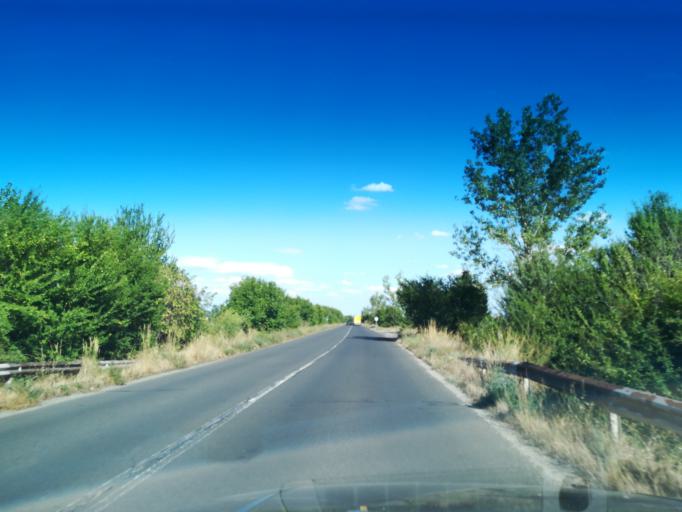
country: BG
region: Stara Zagora
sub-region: Obshtina Chirpan
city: Chirpan
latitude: 42.0717
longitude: 25.2018
